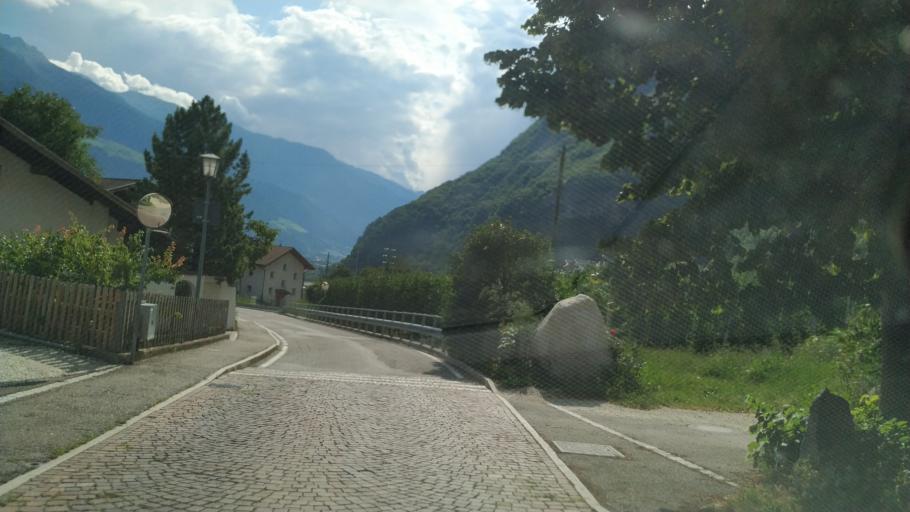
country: IT
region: Trentino-Alto Adige
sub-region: Bolzano
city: Rabla
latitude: 46.6750
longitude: 11.0593
